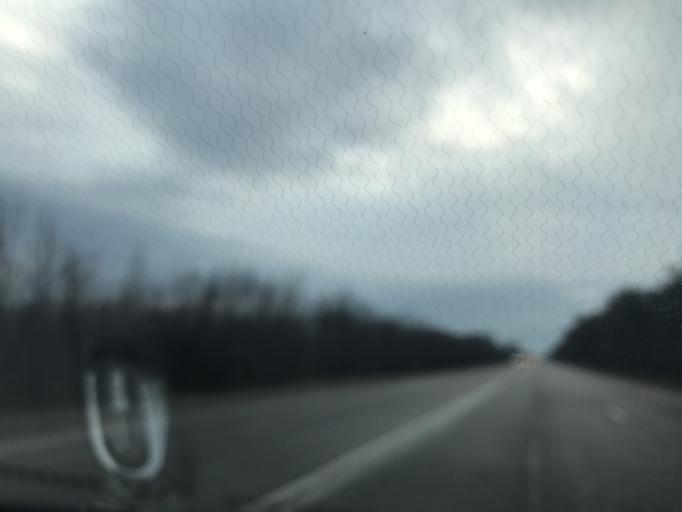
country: RU
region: Krasnodarskiy
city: Tikhoretsk
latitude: 45.8788
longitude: 40.1379
